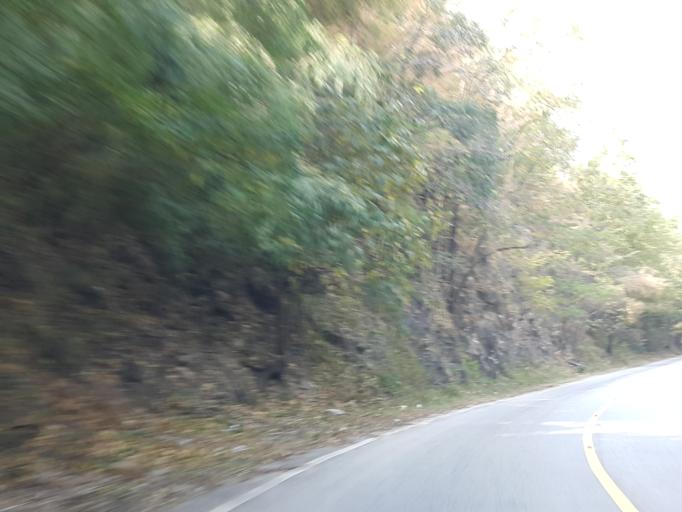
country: TH
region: Chiang Mai
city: Hot
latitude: 18.2252
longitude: 98.4974
